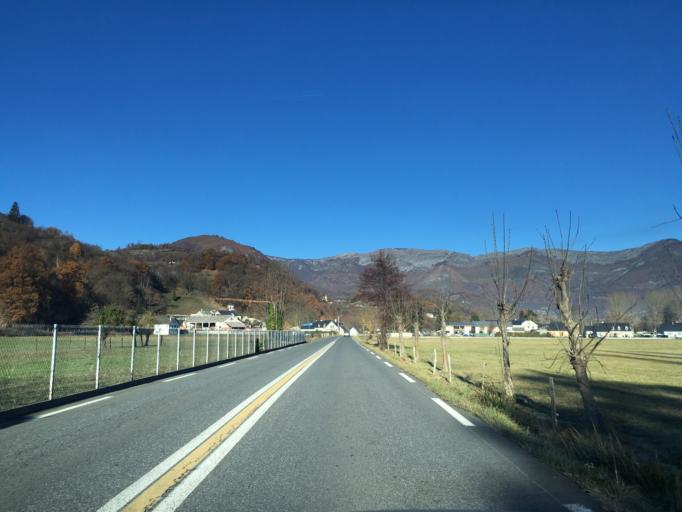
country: FR
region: Midi-Pyrenees
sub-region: Departement des Hautes-Pyrenees
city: Pierrefitte-Nestalas
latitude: 42.9824
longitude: -0.0857
